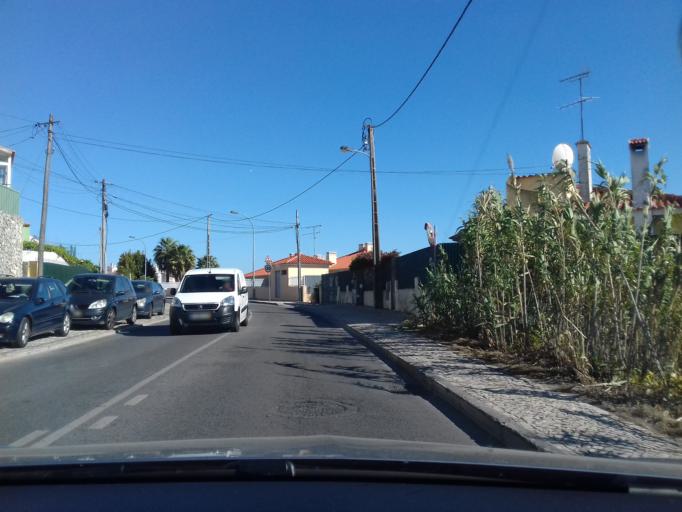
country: PT
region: Lisbon
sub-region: Cascais
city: Alcabideche
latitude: 38.7205
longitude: -9.4114
